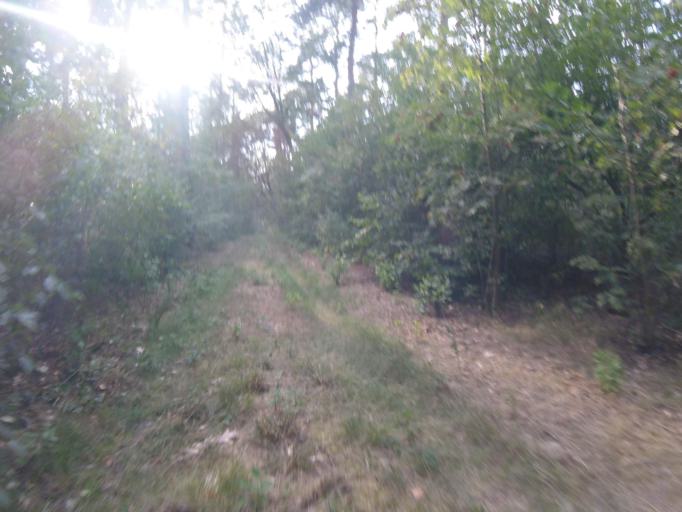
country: DE
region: Brandenburg
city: Gross Koris
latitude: 52.2104
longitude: 13.7167
